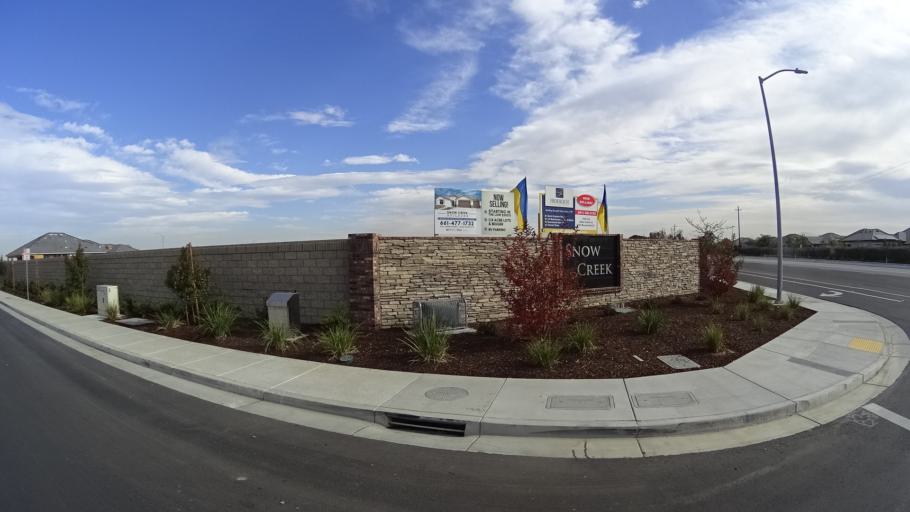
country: US
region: California
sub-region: Kern County
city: Greenacres
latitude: 35.4273
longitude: -119.1011
